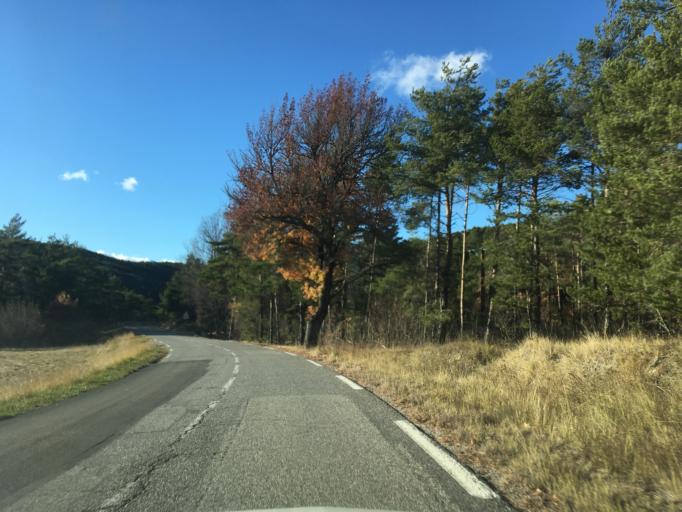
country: FR
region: Provence-Alpes-Cote d'Azur
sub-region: Departement des Alpes-de-Haute-Provence
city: Castellane
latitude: 43.7416
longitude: 6.4831
